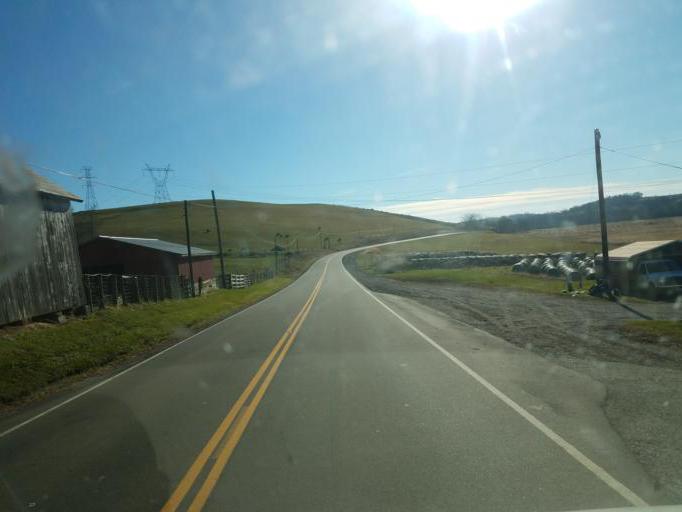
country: US
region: Ohio
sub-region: Muskingum County
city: Dresden
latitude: 40.2081
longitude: -82.0535
